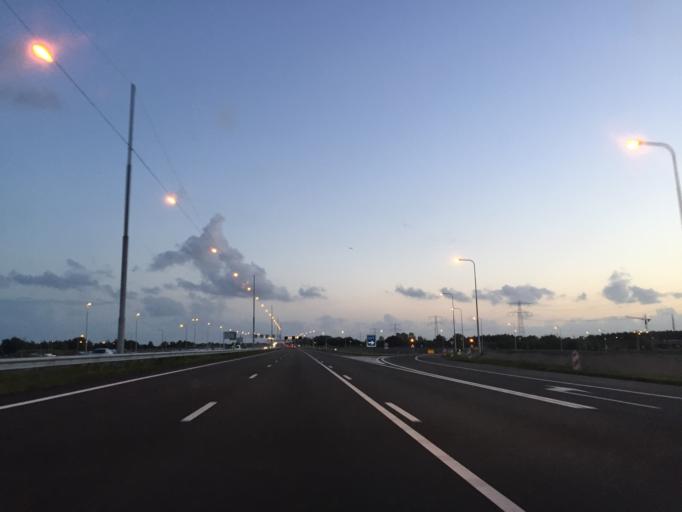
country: NL
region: North Holland
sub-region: Gemeente Naarden
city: Naarden
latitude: 52.3354
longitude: 5.1583
